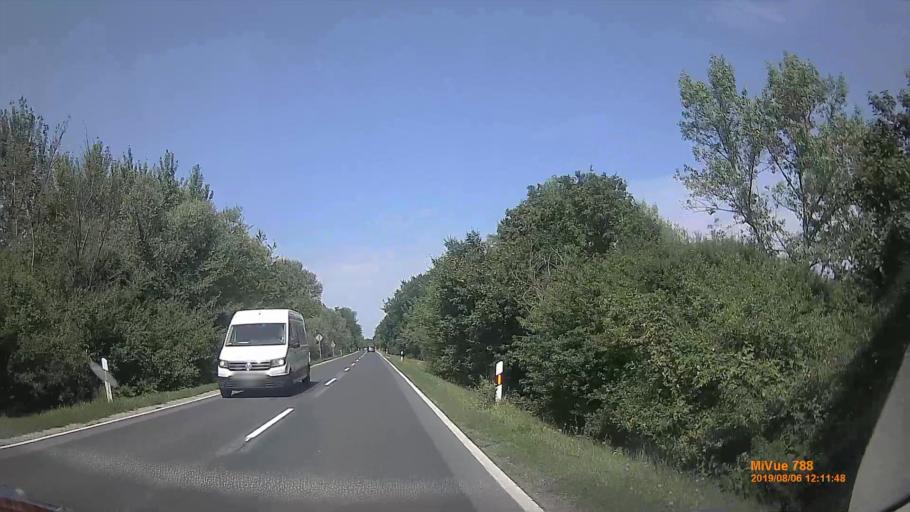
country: HU
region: Vas
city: Vasvar
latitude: 47.1170
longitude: 16.8575
